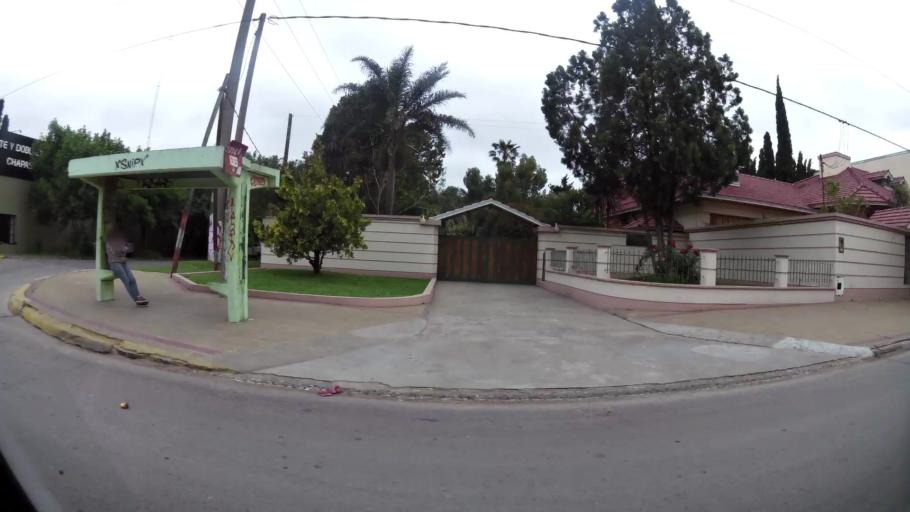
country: AR
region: Buenos Aires
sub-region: Partido de La Plata
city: La Plata
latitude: -34.9468
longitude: -57.9948
